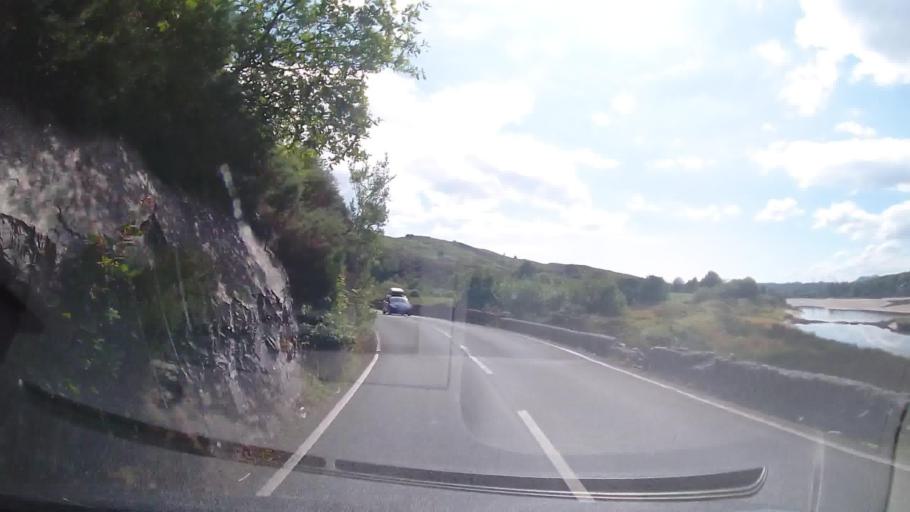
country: GB
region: Wales
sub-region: Gwynedd
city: Penrhyndeudraeth
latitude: 52.9264
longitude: -4.0440
